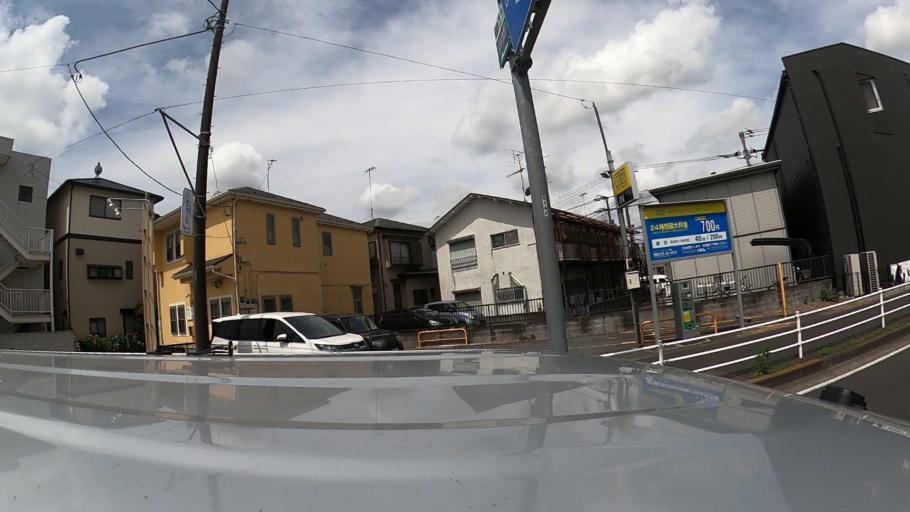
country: JP
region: Kanagawa
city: Minami-rinkan
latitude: 35.4150
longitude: 139.4698
